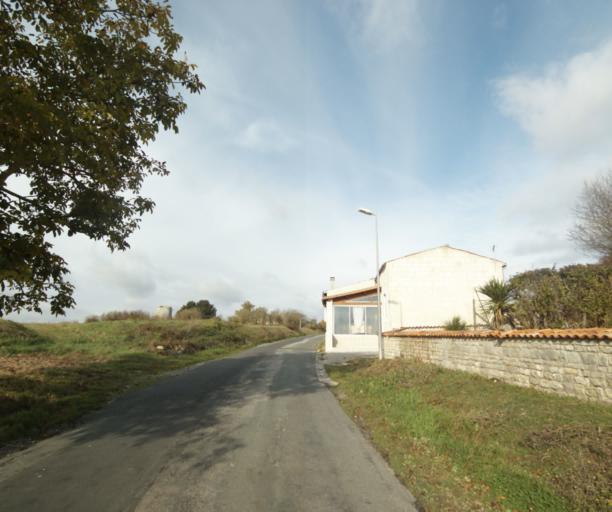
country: FR
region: Poitou-Charentes
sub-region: Departement de la Charente-Maritime
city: Saint-Georges-des-Coteaux
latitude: 45.7596
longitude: -0.7119
